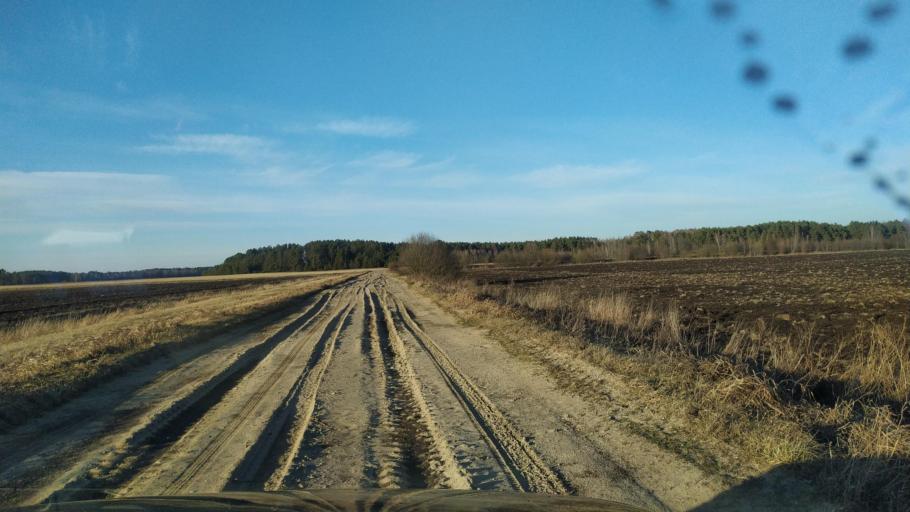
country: BY
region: Brest
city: Pruzhany
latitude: 52.5509
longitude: 24.3029
